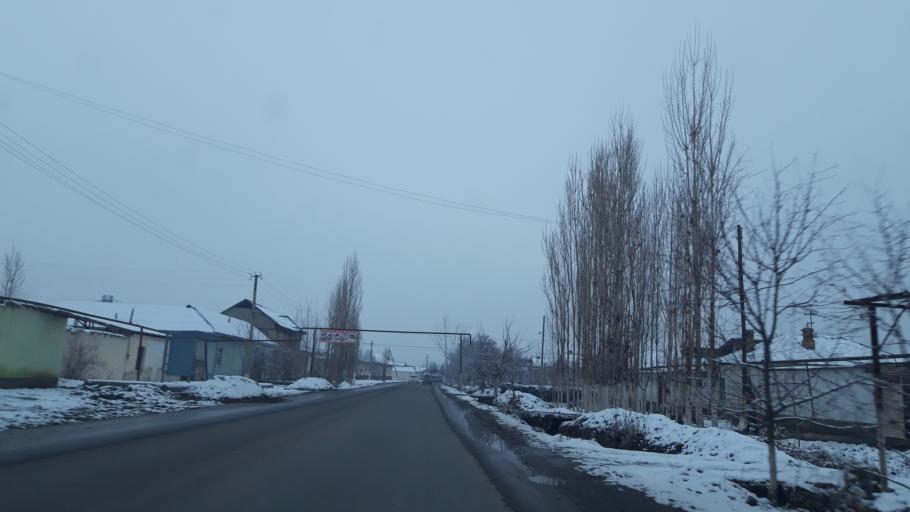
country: UZ
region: Andijon
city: Asaka
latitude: 40.6350
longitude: 72.2074
